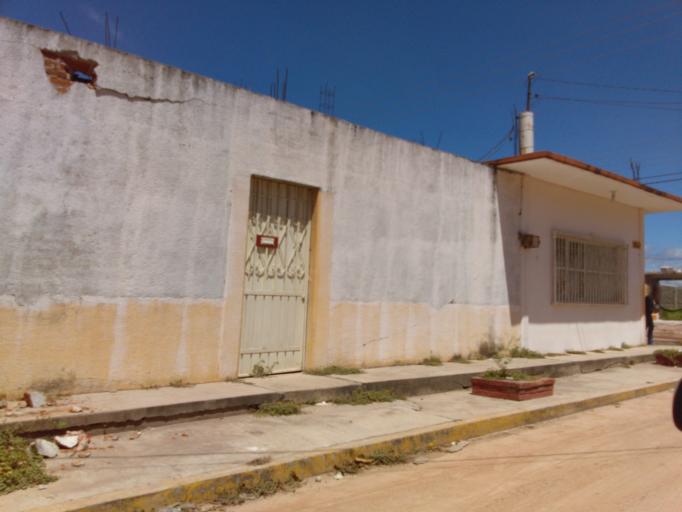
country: MX
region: Oaxaca
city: Asuncion Ixtaltepec
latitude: 16.5022
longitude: -95.0597
